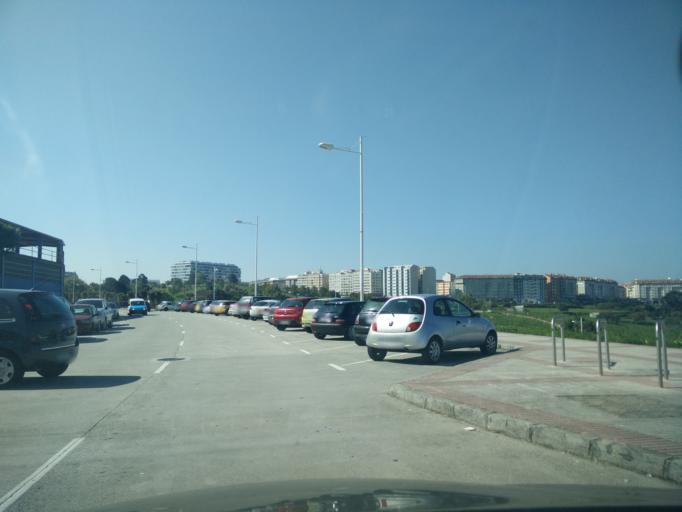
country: ES
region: Galicia
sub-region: Provincia da Coruna
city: A Coruna
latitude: 43.3458
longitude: -8.3895
